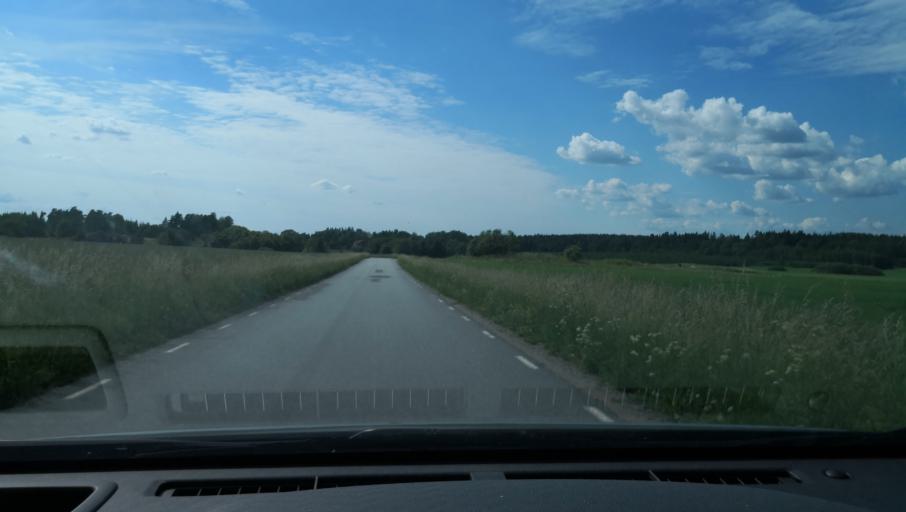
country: SE
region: Uppsala
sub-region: Enkopings Kommun
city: Orsundsbro
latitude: 59.8139
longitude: 17.3759
